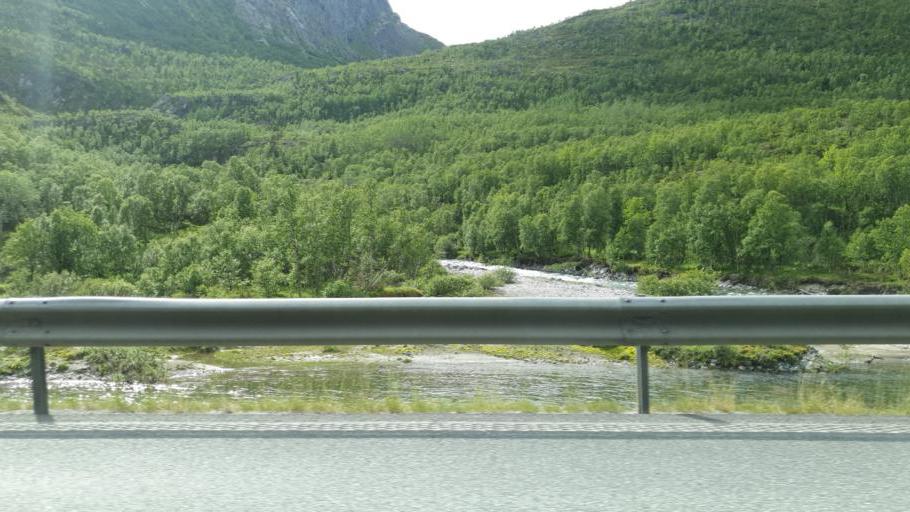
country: NO
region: Sor-Trondelag
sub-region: Oppdal
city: Oppdal
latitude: 62.3767
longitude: 9.6397
